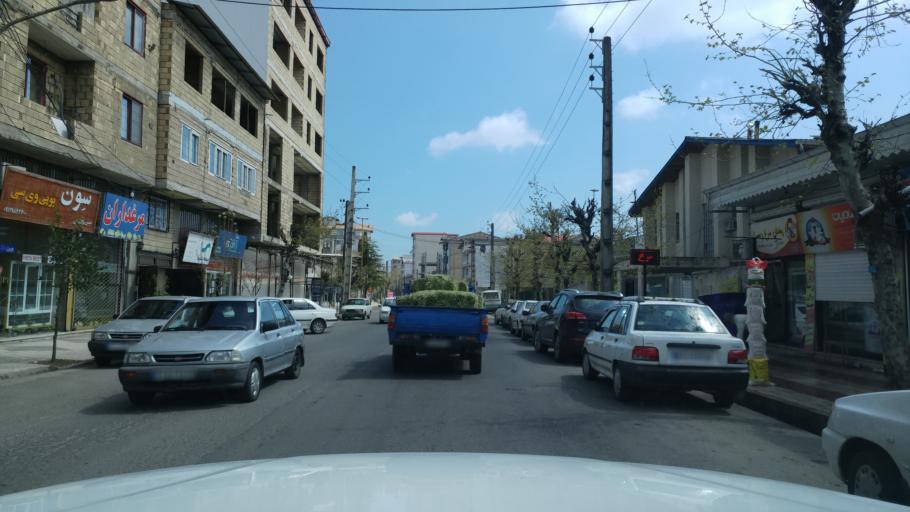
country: IR
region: Gilan
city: Hashtpar
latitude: 37.7932
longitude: 48.9055
